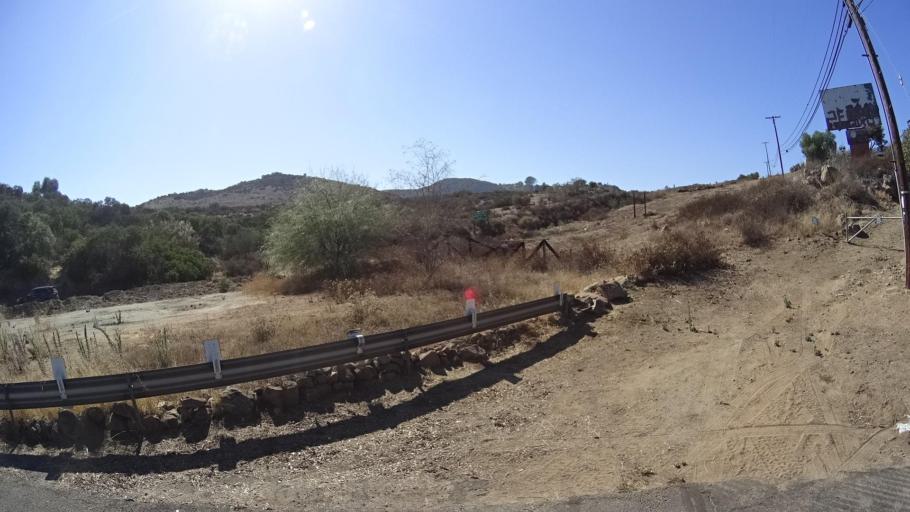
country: US
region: California
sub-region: San Diego County
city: Hidden Meadows
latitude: 33.2470
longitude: -117.1504
